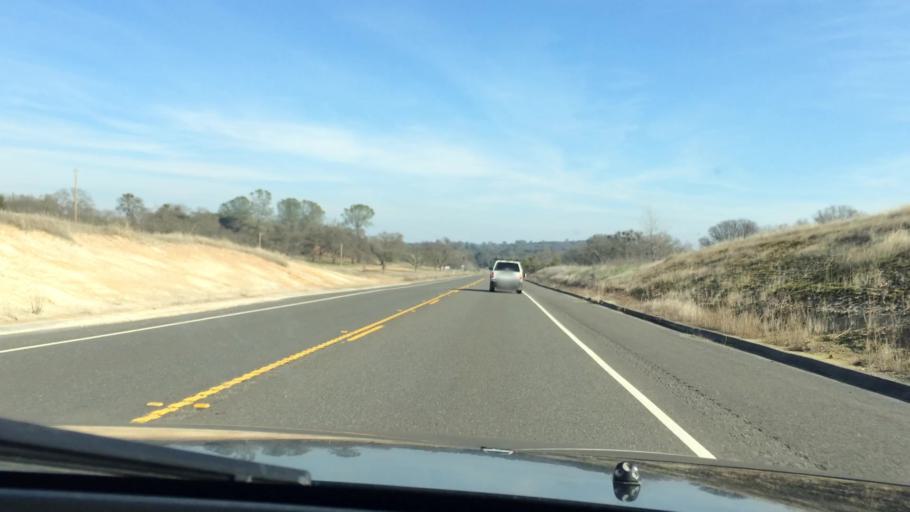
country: US
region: California
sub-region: Sacramento County
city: Rancho Murieta
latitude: 38.4808
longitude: -121.0337
